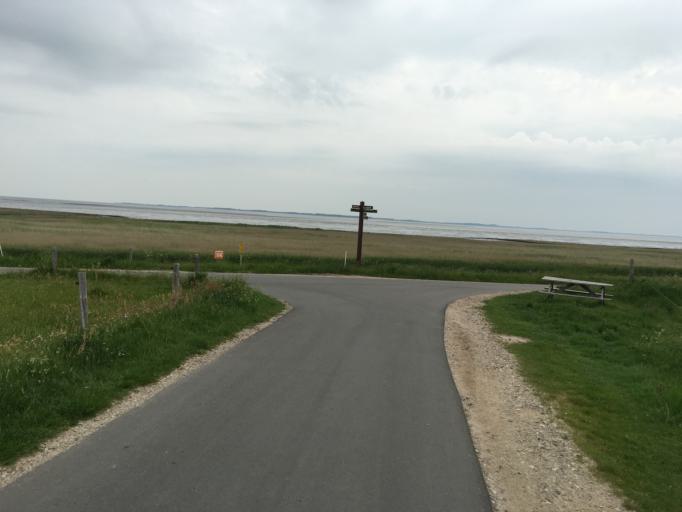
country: DE
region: Schleswig-Holstein
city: Norddorf
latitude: 54.6787
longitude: 8.3417
